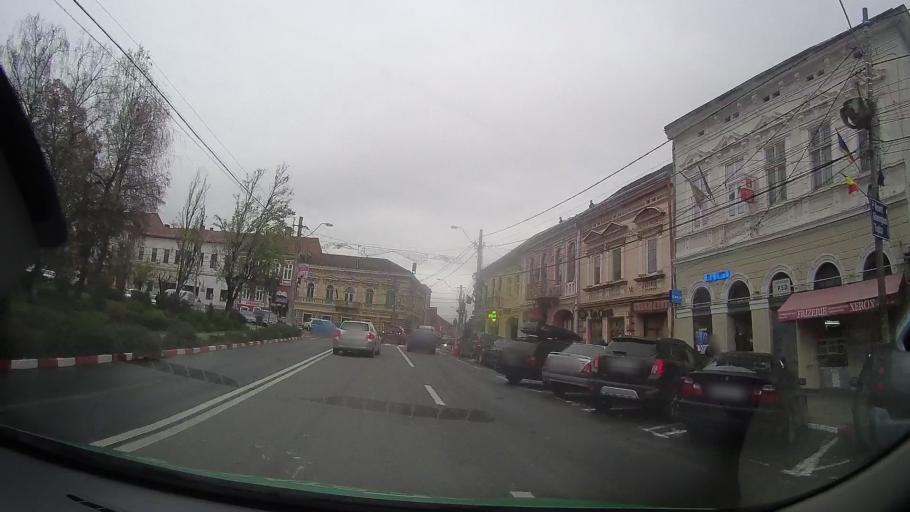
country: RO
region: Mures
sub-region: Municipiul Reghin
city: Reghin
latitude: 46.7819
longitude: 24.7017
